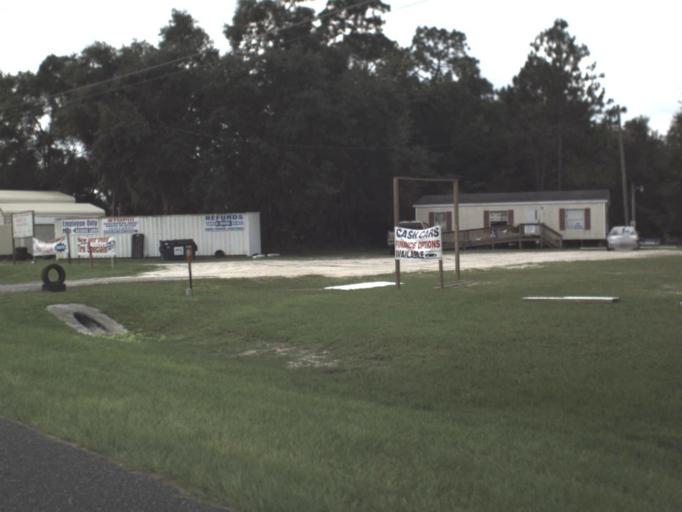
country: US
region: Florida
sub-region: Levy County
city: Bronson
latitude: 29.4390
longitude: -82.6231
